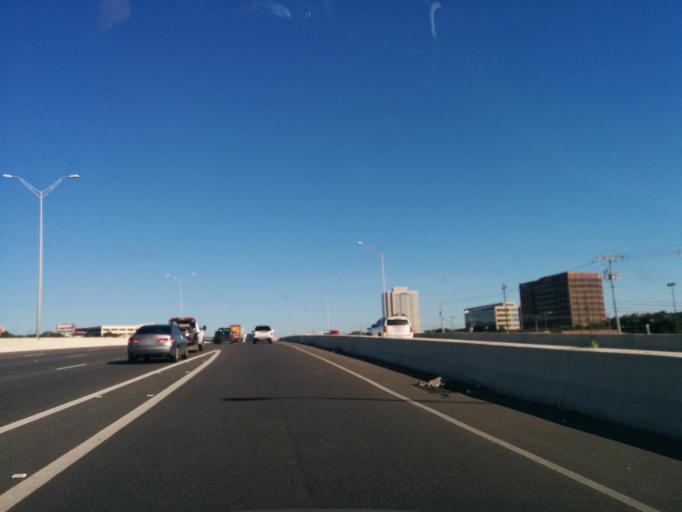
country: US
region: Texas
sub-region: Bexar County
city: Balcones Heights
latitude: 29.5301
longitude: -98.5608
